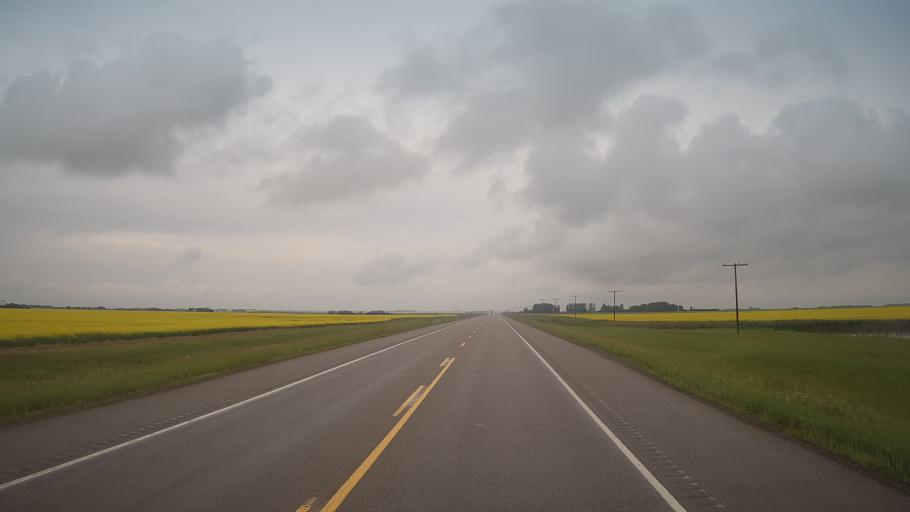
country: CA
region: Saskatchewan
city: Unity
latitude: 52.4350
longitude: -108.9552
